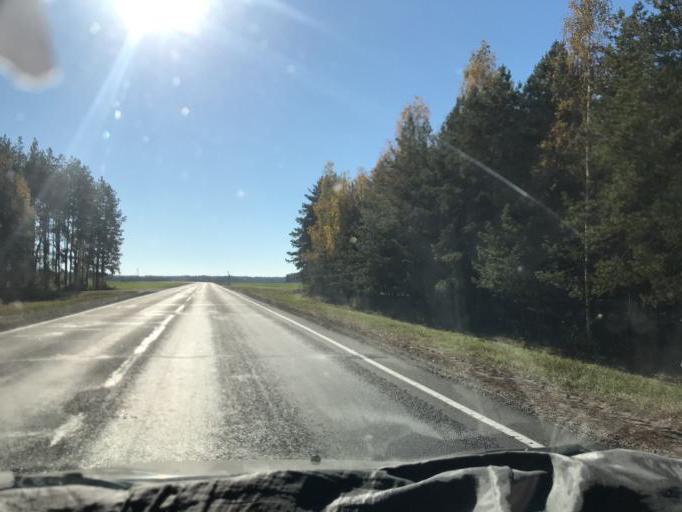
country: BY
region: Gomel
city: Parychy
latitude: 52.8777
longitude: 29.3156
